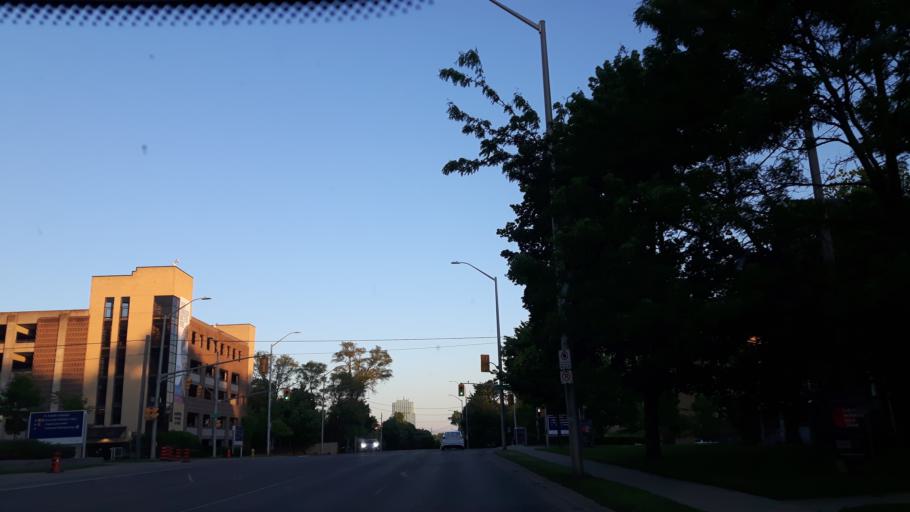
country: CA
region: Ontario
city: London
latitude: 43.0002
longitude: -81.2557
